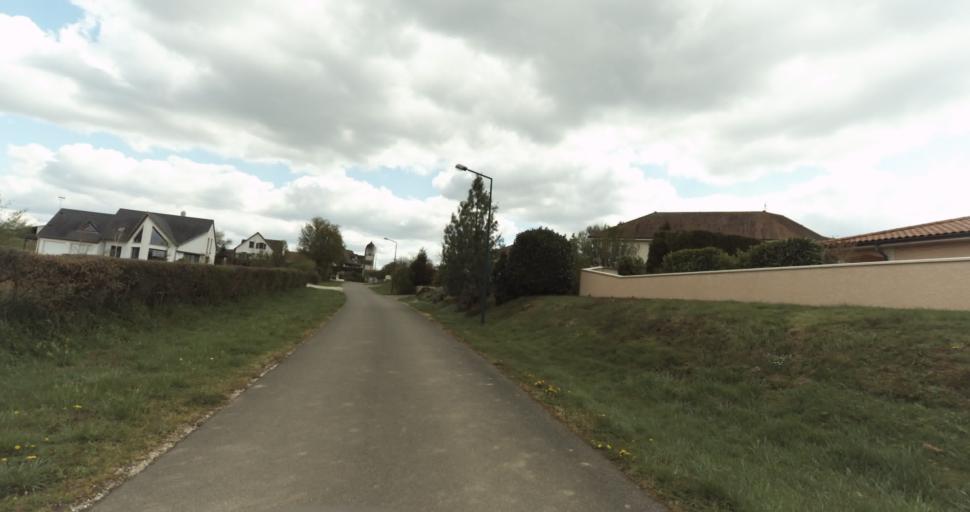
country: FR
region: Franche-Comte
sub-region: Departement du Jura
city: Champvans
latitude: 47.1470
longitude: 5.4286
